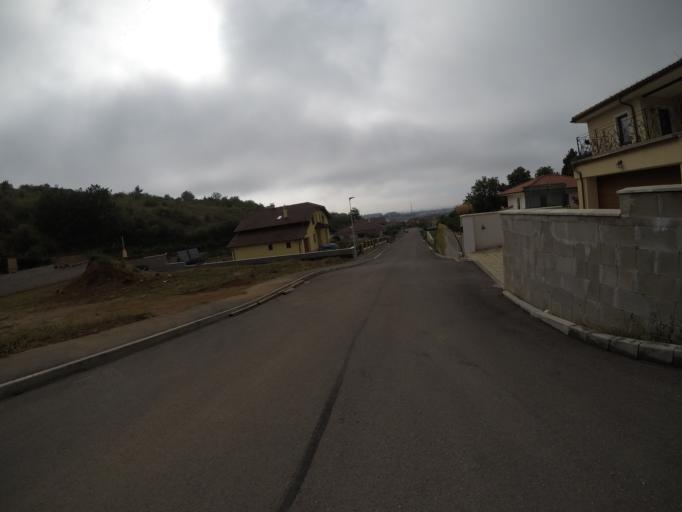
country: SK
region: Trenciansky
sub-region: Okres Nove Mesto nad Vahom
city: Nove Mesto nad Vahom
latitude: 48.7602
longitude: 17.8110
